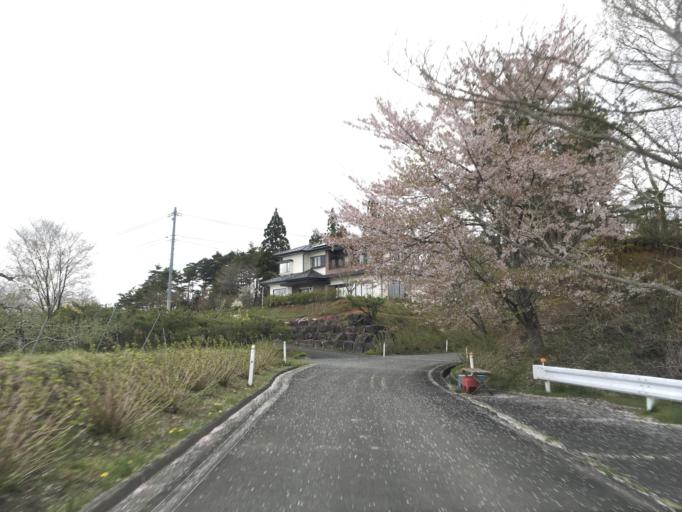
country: JP
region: Iwate
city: Ichinoseki
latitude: 38.8531
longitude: 141.3288
